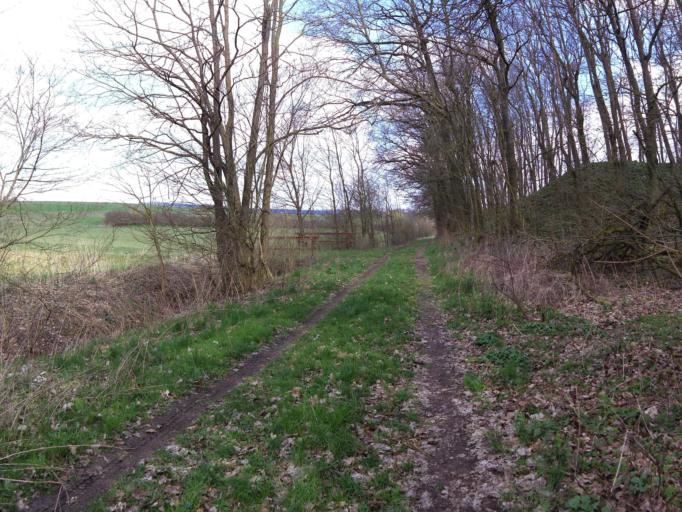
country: DE
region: Bavaria
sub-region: Regierungsbezirk Unterfranken
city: Biebelried
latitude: 49.7442
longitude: 10.1000
